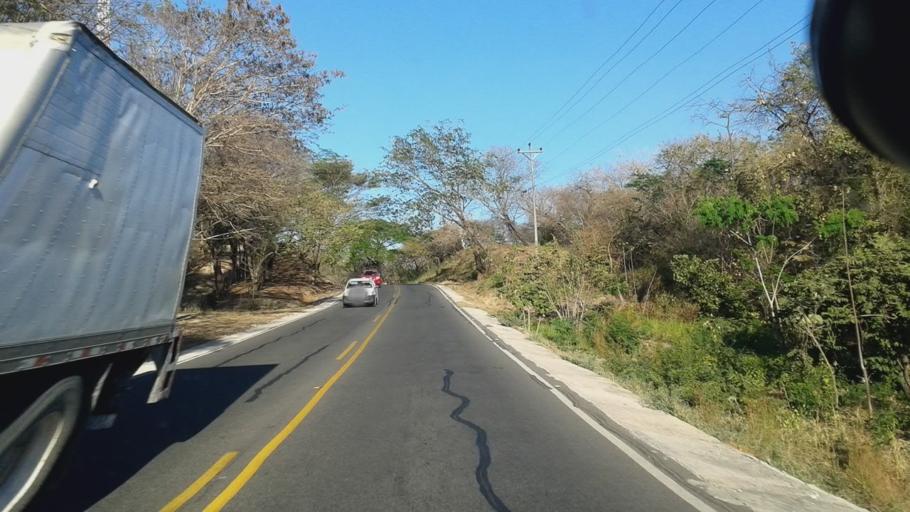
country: CR
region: Guanacaste
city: Nandayure
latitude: 10.2213
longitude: -85.1993
